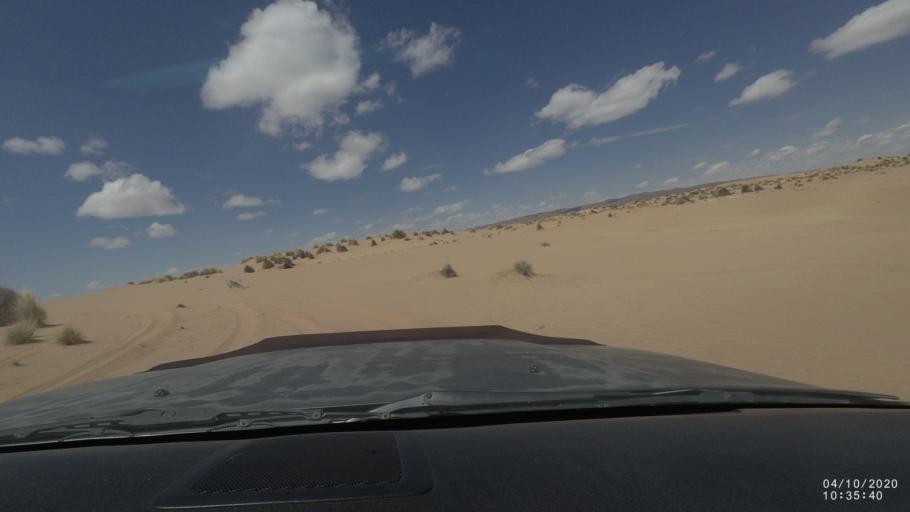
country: BO
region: Oruro
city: Poopo
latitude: -18.7057
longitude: -67.4748
